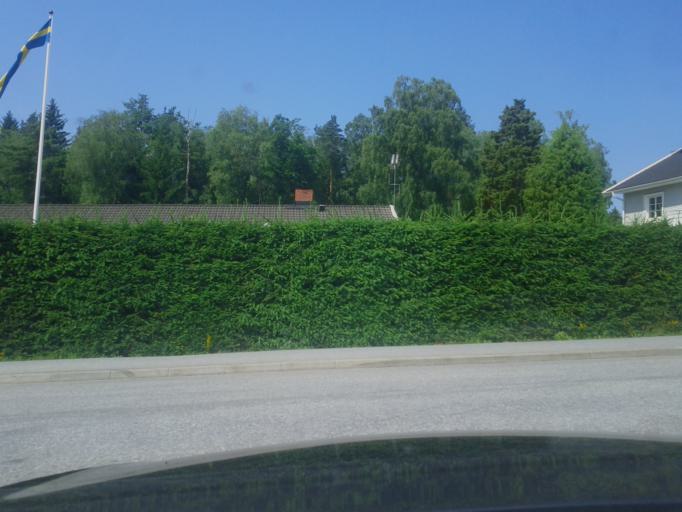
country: SE
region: Stockholm
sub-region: Vallentuna Kommun
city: Vallentuna
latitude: 59.5014
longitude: 18.0923
